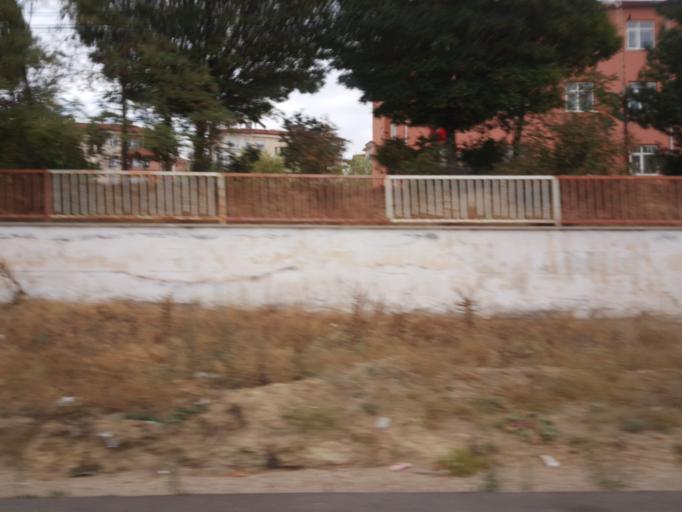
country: TR
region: Kirikkale
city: Keskin
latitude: 39.6776
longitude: 33.5994
